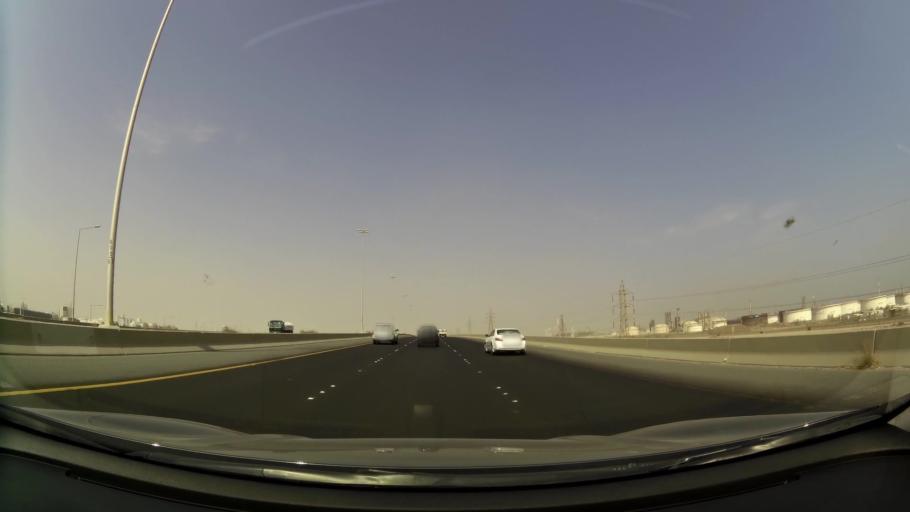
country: KW
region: Al Ahmadi
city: Al Fahahil
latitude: 29.0090
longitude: 48.1339
